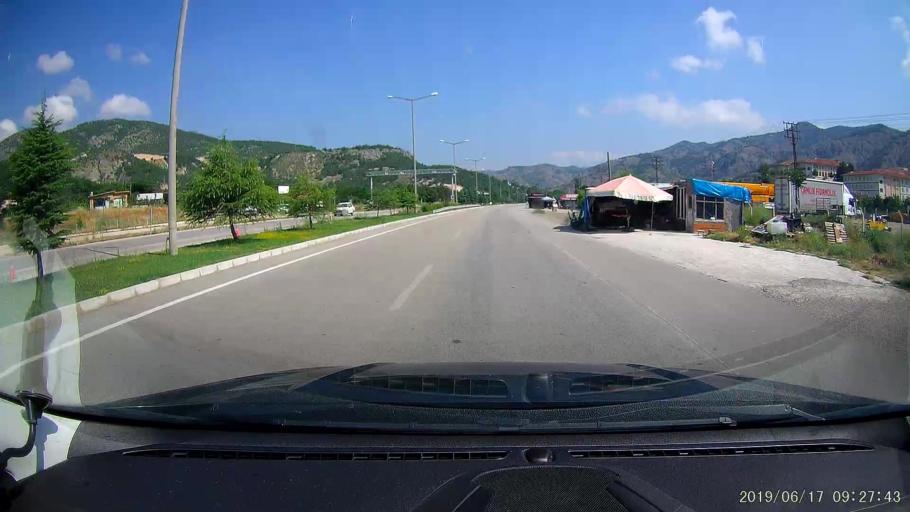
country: TR
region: Amasya
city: Amasya
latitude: 40.6801
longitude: 35.8247
